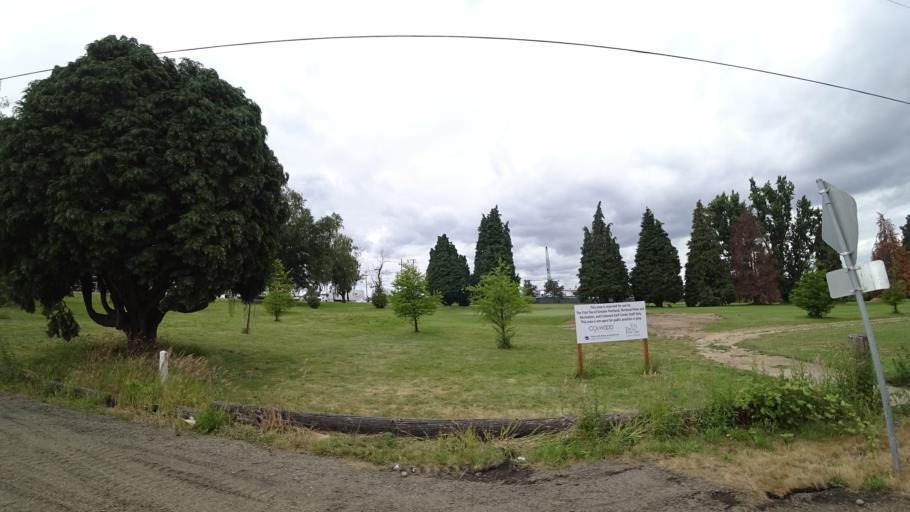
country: US
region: Oregon
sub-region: Multnomah County
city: Lents
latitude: 45.5671
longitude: -122.5884
